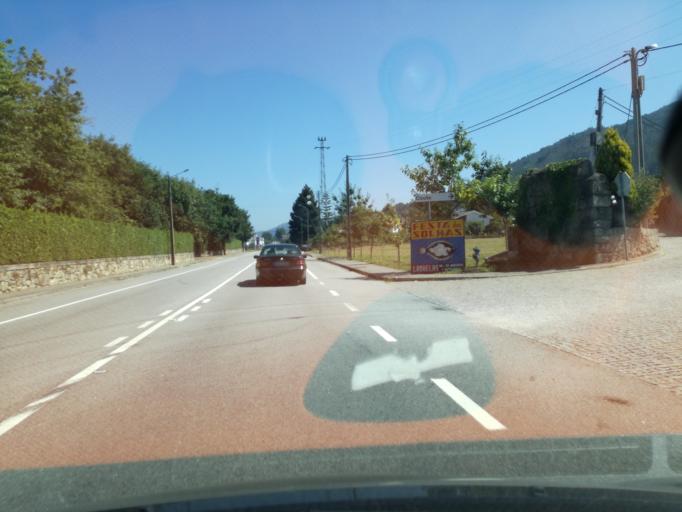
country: ES
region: Galicia
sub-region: Provincia de Pontevedra
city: O Rosal
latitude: 41.9071
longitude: -8.7958
